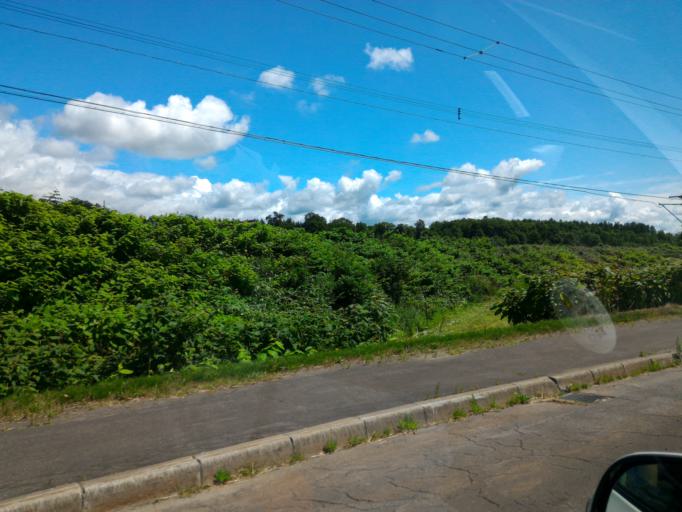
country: JP
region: Hokkaido
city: Nayoro
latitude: 44.5075
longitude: 142.3341
